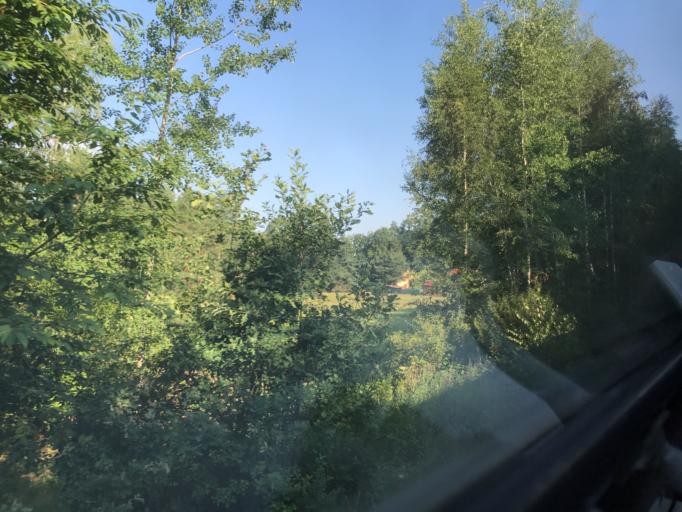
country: CZ
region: Jihocesky
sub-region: Okres Tabor
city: Veseli nad Luznici
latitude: 49.1467
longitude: 14.7291
